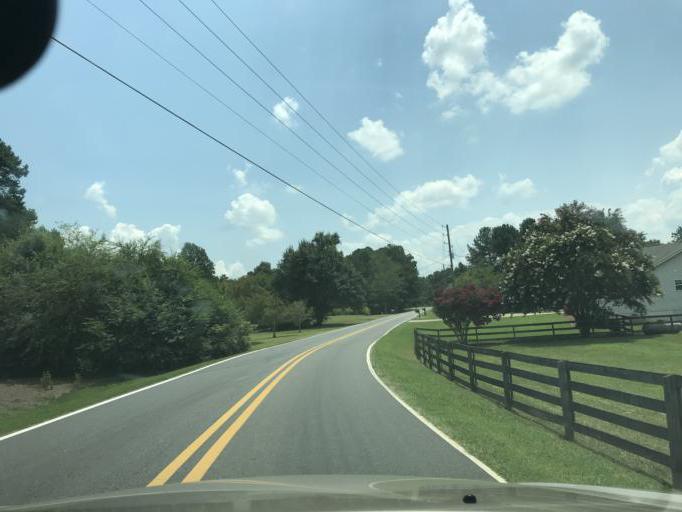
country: US
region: Georgia
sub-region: Forsyth County
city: Cumming
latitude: 34.3105
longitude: -84.1936
